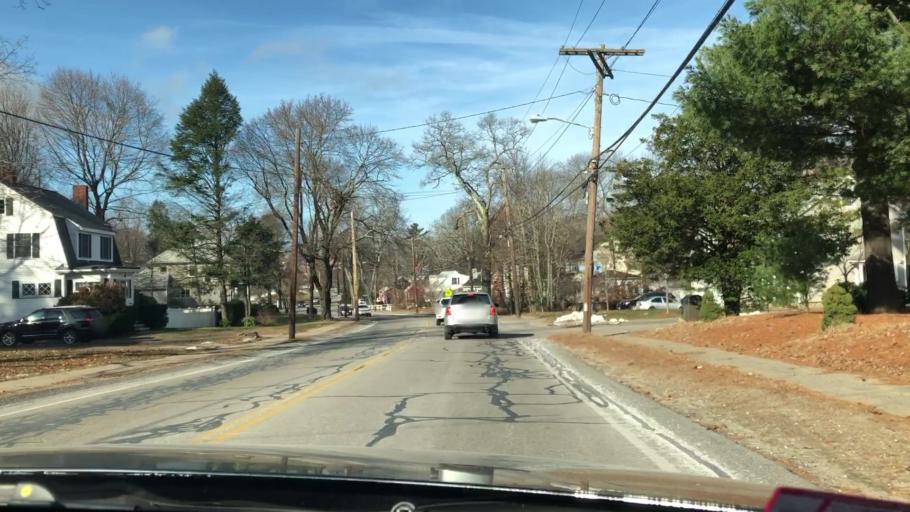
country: US
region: Massachusetts
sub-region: Norfolk County
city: Walpole
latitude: 42.1333
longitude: -71.2442
